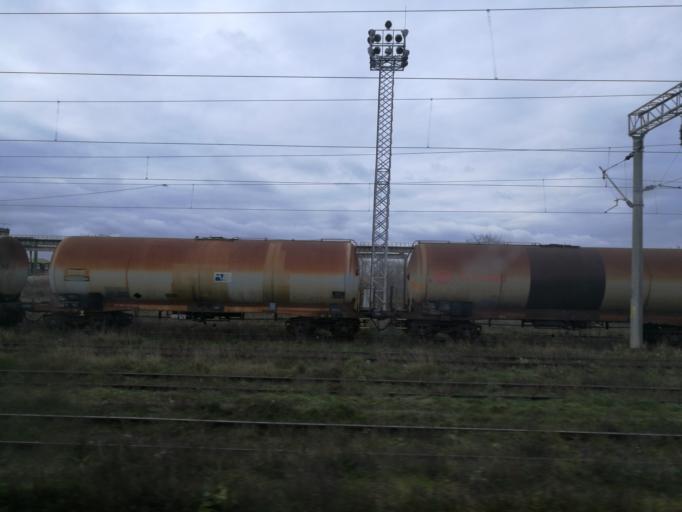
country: RO
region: Neamt
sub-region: Municipiul Roman
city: Roman
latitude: 46.9410
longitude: 26.9179
